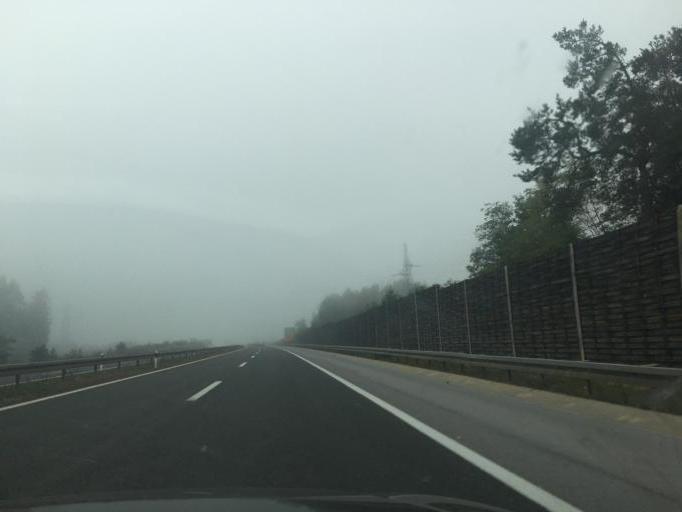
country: HR
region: Licko-Senjska
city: Gospic
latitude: 44.5824
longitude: 15.4299
